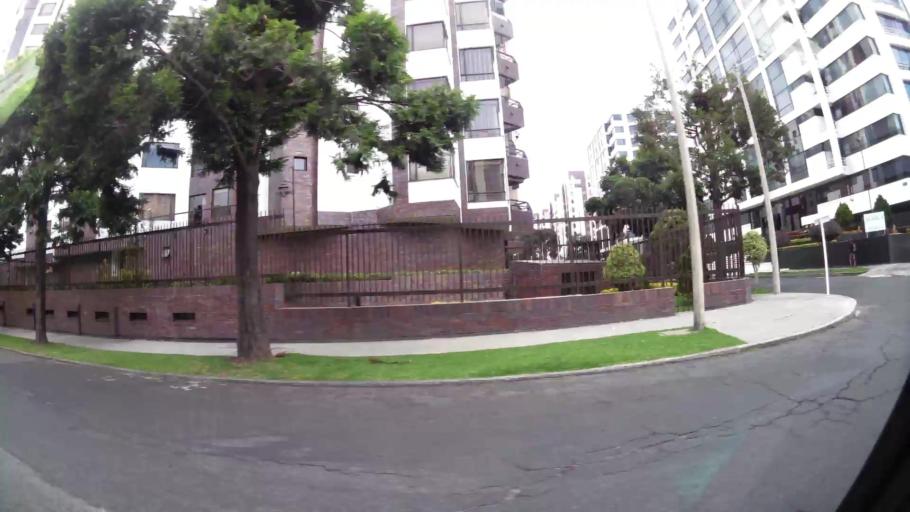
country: CO
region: Bogota D.C.
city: Barrio San Luis
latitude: 4.7007
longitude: -74.0352
